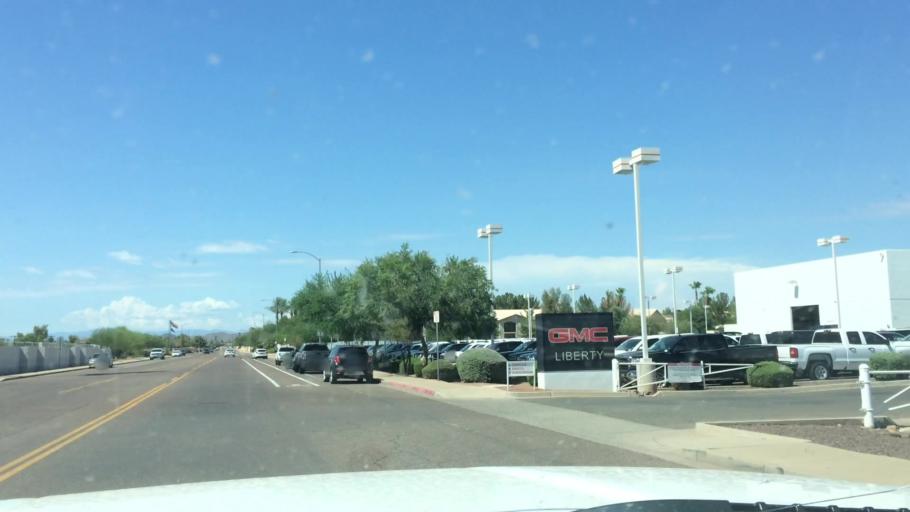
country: US
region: Arizona
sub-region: Maricopa County
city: Sun City
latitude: 33.6387
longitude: -112.2463
